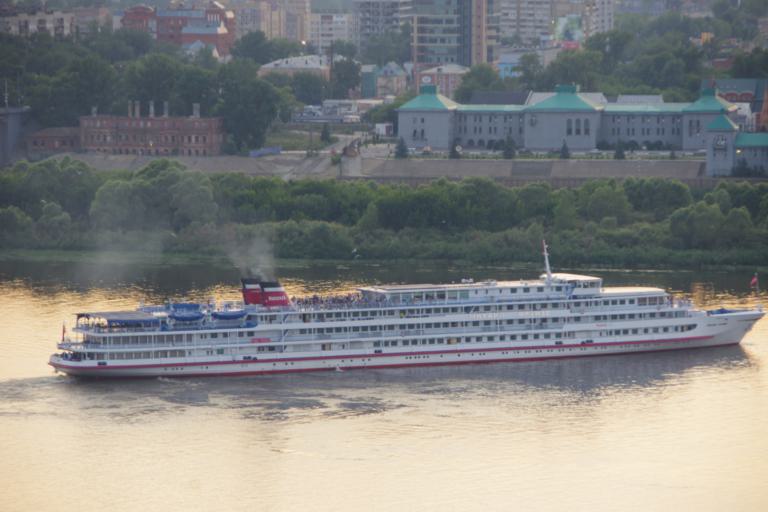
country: RU
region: Nizjnij Novgorod
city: Nizhniy Novgorod
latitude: 56.3262
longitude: 43.9869
